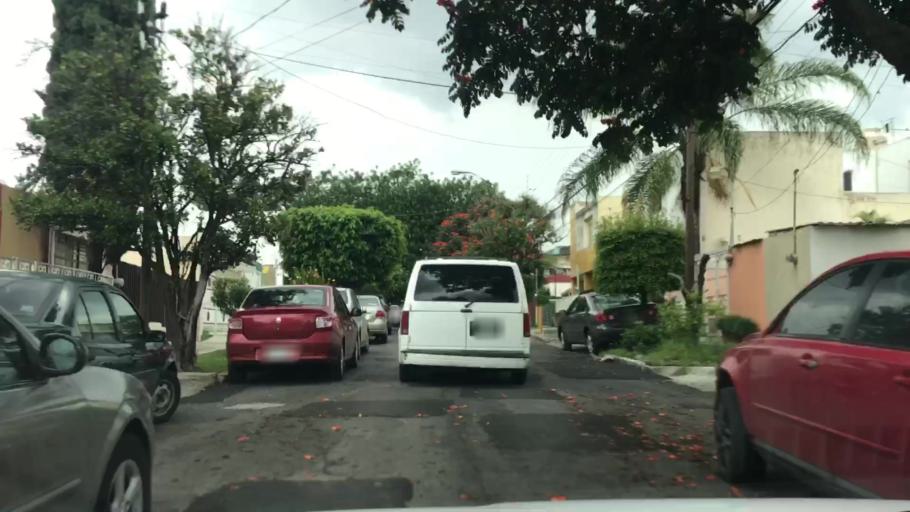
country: MX
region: Jalisco
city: Guadalajara
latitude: 20.6246
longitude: -103.4105
